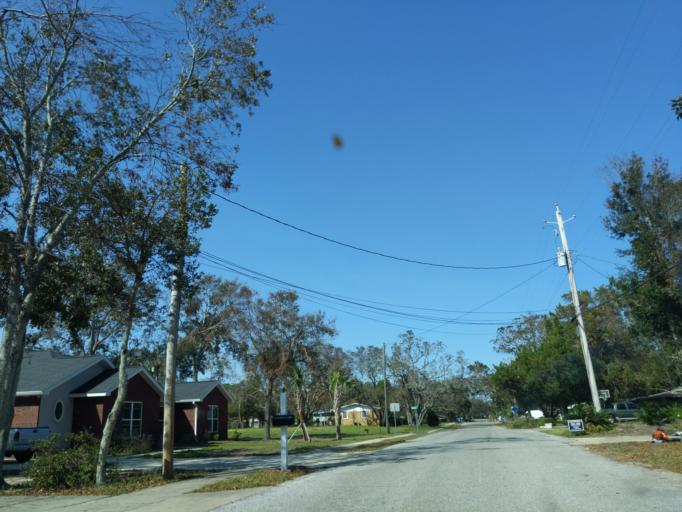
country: US
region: Florida
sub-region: Santa Rosa County
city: Gulf Breeze
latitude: 30.3568
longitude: -87.1866
